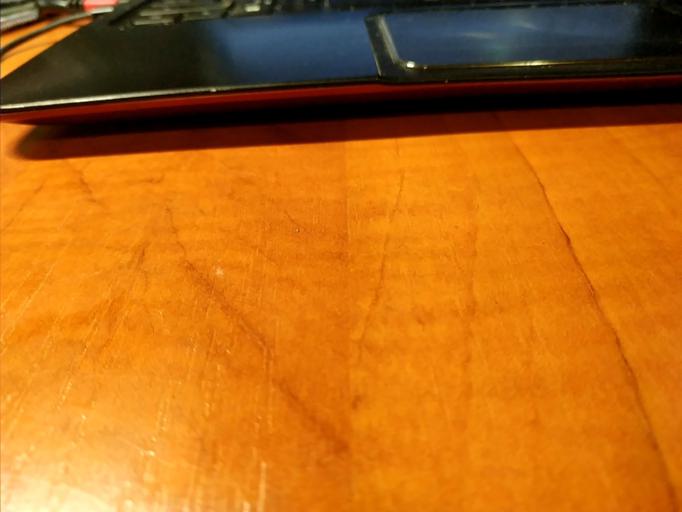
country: RU
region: Tverskaya
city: Ves'yegonsk
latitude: 58.8143
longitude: 37.5435
